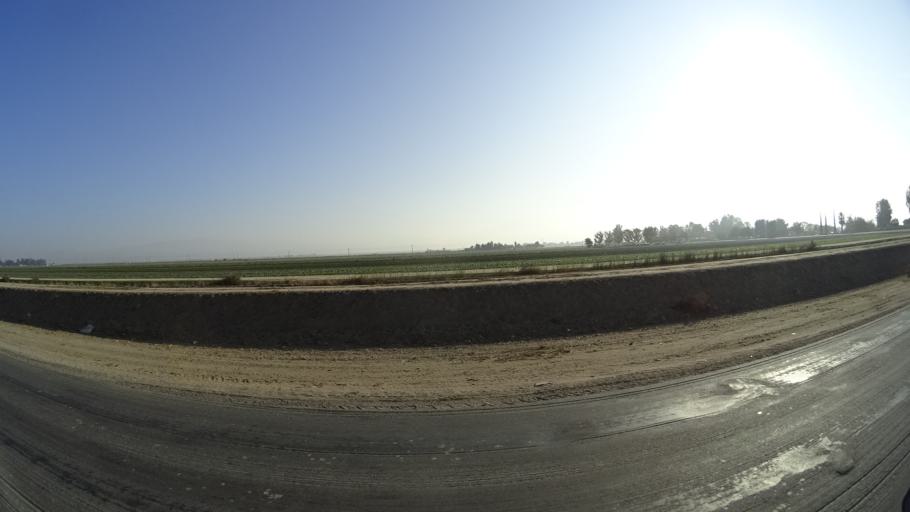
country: US
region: California
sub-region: Kern County
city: Greenfield
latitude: 35.2539
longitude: -118.9852
